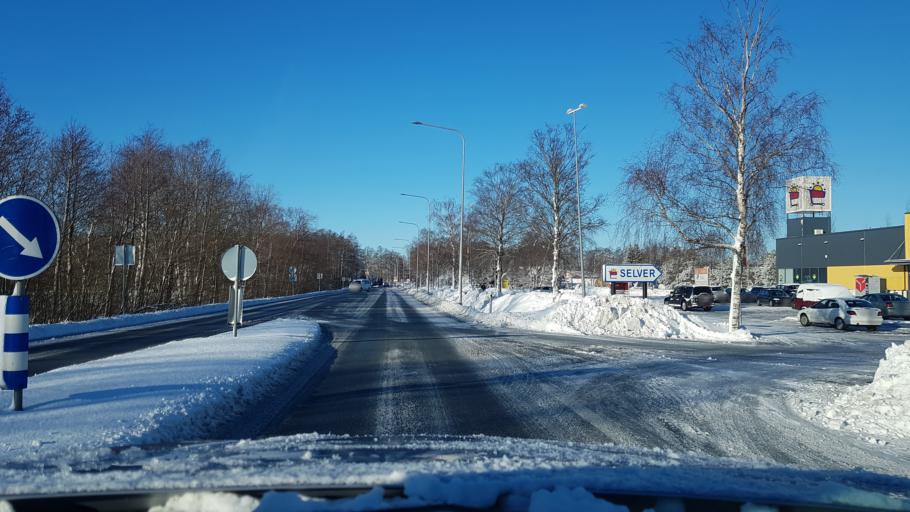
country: EE
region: Hiiumaa
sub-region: Kaerdla linn
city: Kardla
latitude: 58.9890
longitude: 22.7646
